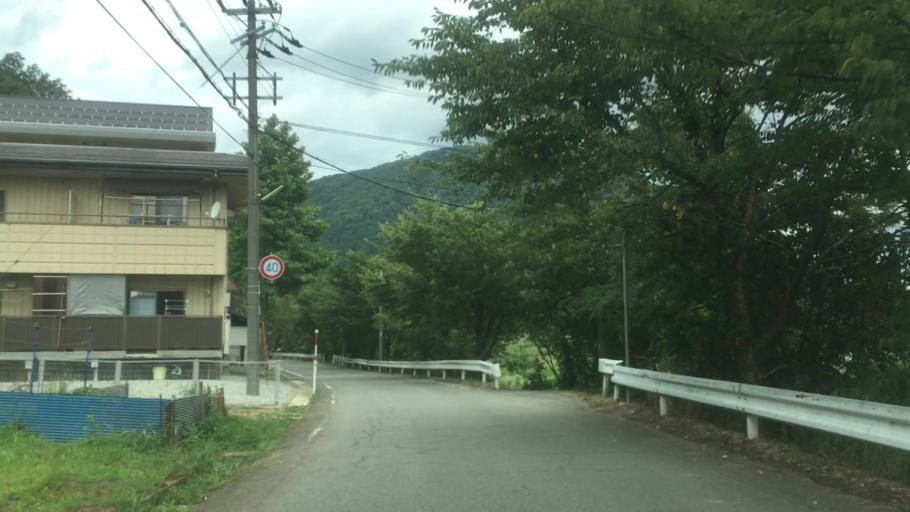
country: JP
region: Hyogo
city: Toyooka
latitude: 35.6011
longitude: 134.8014
